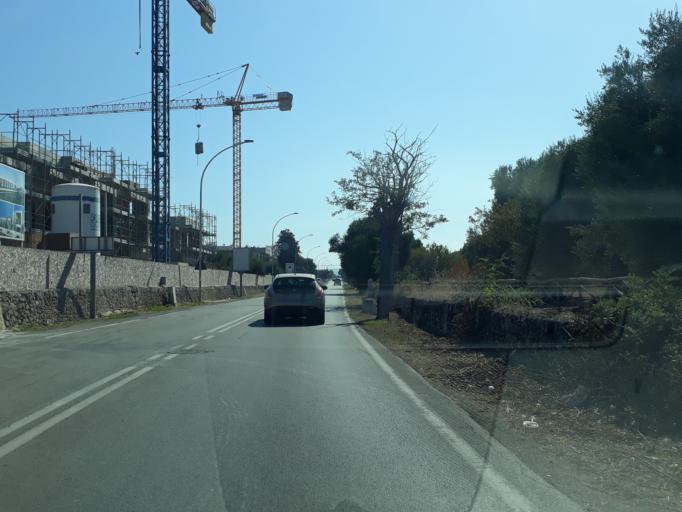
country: IT
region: Apulia
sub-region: Provincia di Bari
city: Monopoli
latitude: 40.9389
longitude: 17.3076
